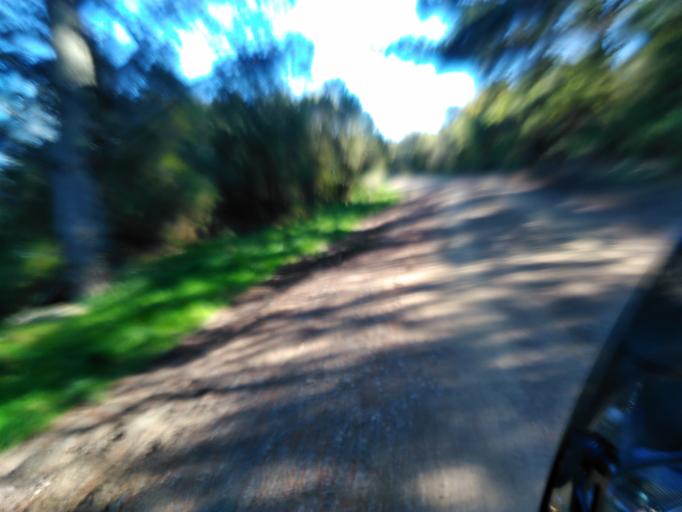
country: NZ
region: Gisborne
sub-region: Gisborne District
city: Gisborne
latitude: -38.3886
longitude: 177.6256
